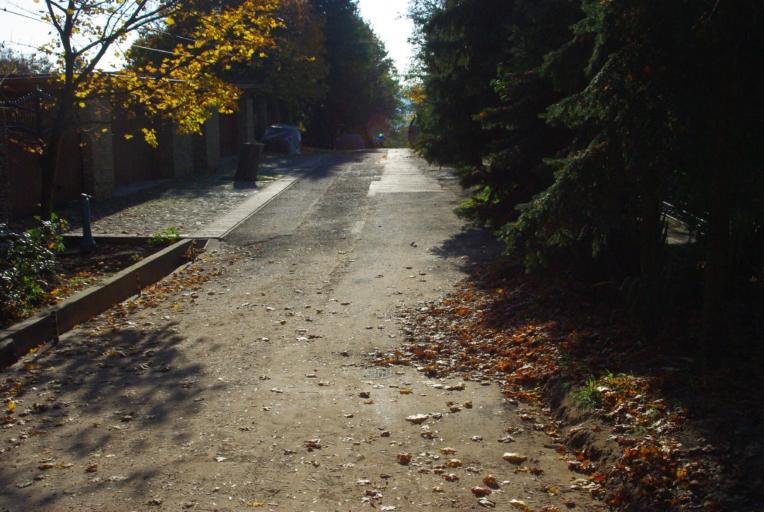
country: HU
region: Pest
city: Piliscsaba
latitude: 47.6433
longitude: 18.8363
